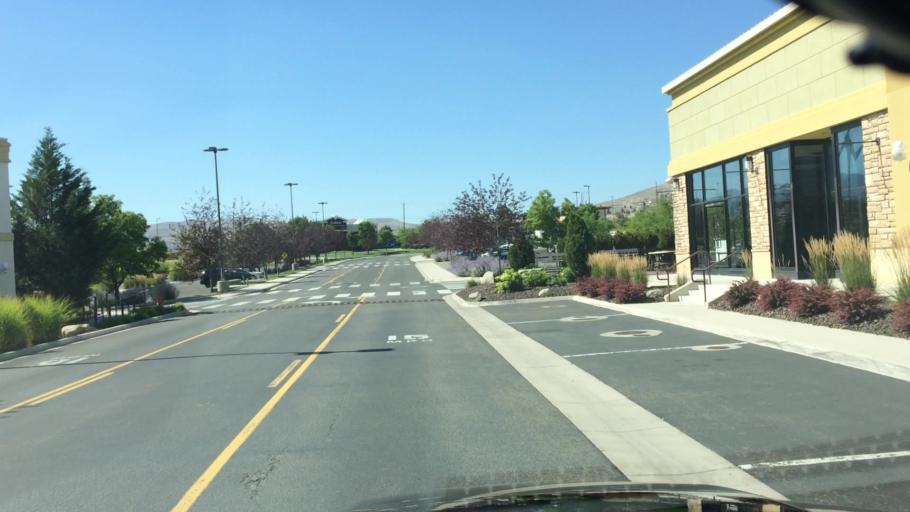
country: US
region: Nevada
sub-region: Washoe County
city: Sparks
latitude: 39.4037
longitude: -119.7505
